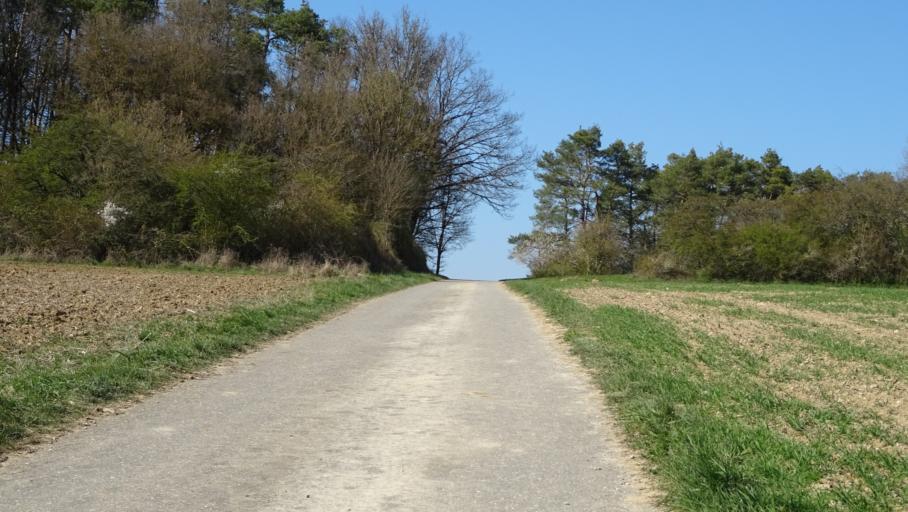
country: DE
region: Baden-Wuerttemberg
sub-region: Karlsruhe Region
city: Limbach
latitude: 49.4165
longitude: 9.2434
